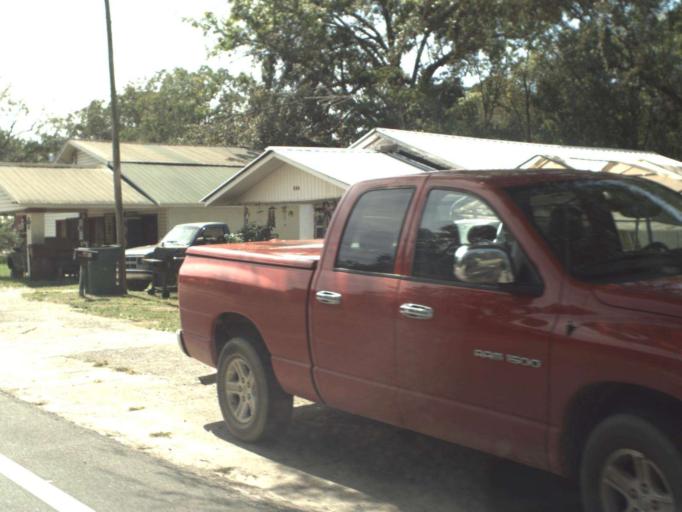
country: US
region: Florida
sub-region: Washington County
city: Chipley
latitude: 30.7909
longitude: -85.5391
